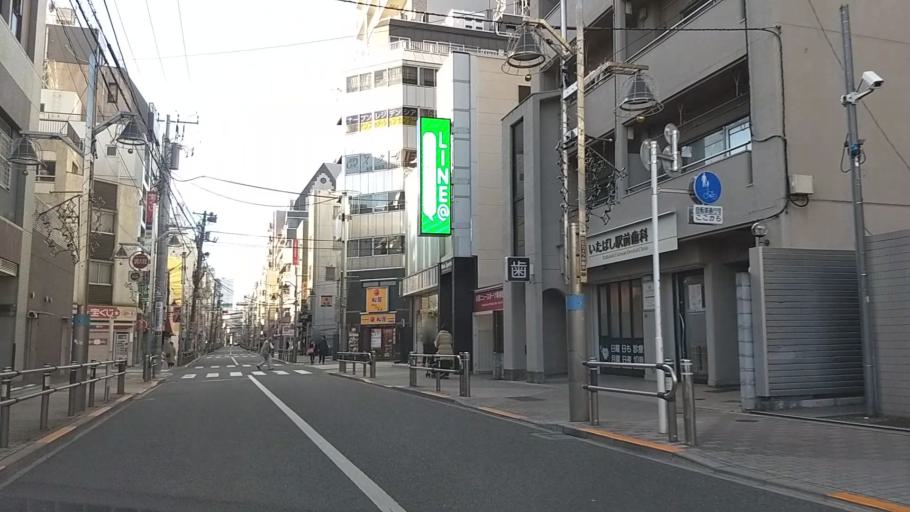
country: JP
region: Saitama
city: Kawaguchi
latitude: 35.7468
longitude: 139.7199
